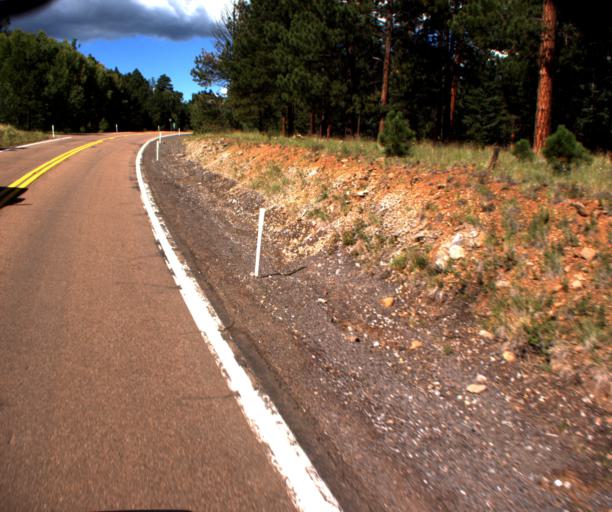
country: US
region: Arizona
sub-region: Apache County
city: Eagar
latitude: 34.0579
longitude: -109.4993
